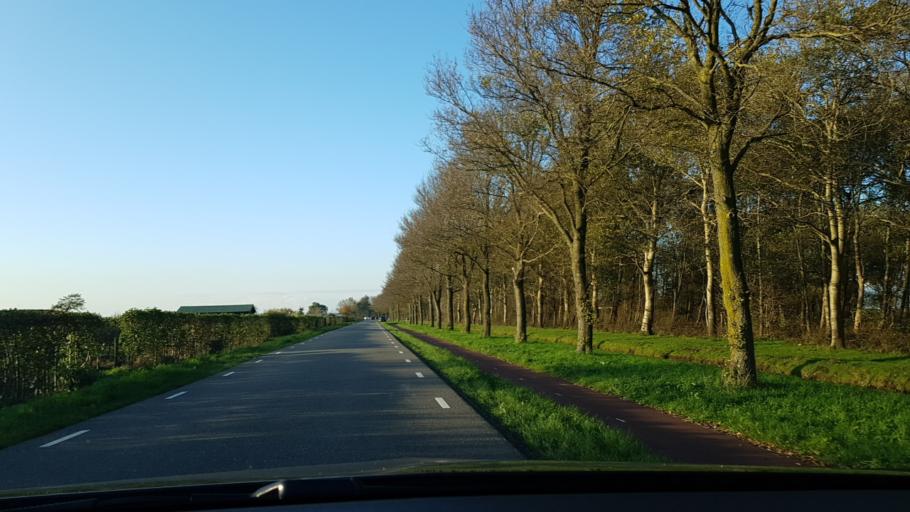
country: NL
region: North Holland
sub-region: Gemeente Uitgeest
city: Uitgeest
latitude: 52.4669
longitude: 4.7317
